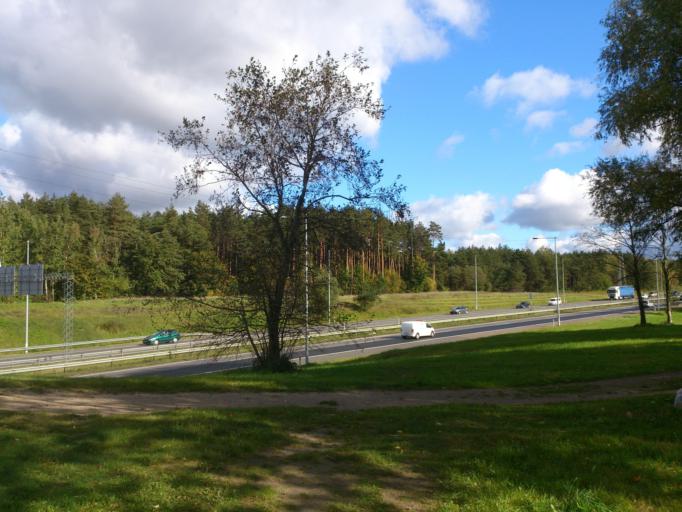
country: LT
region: Kauno apskritis
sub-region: Kaunas
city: Eiguliai
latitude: 54.9351
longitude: 23.9285
